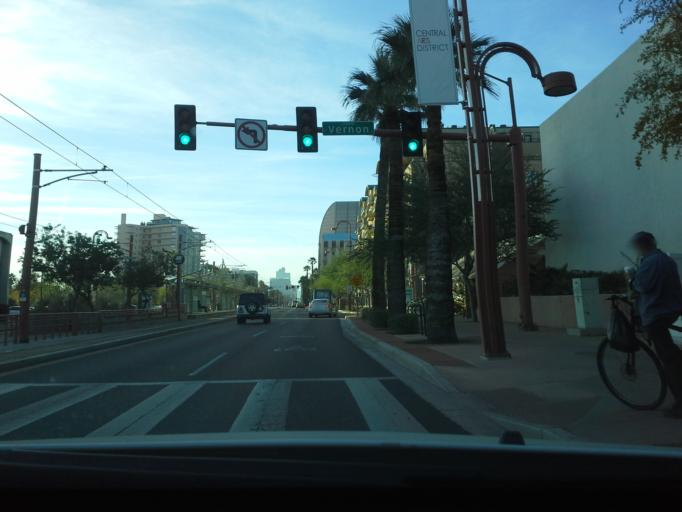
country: US
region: Arizona
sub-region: Maricopa County
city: Phoenix
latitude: 33.4746
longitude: -112.0737
